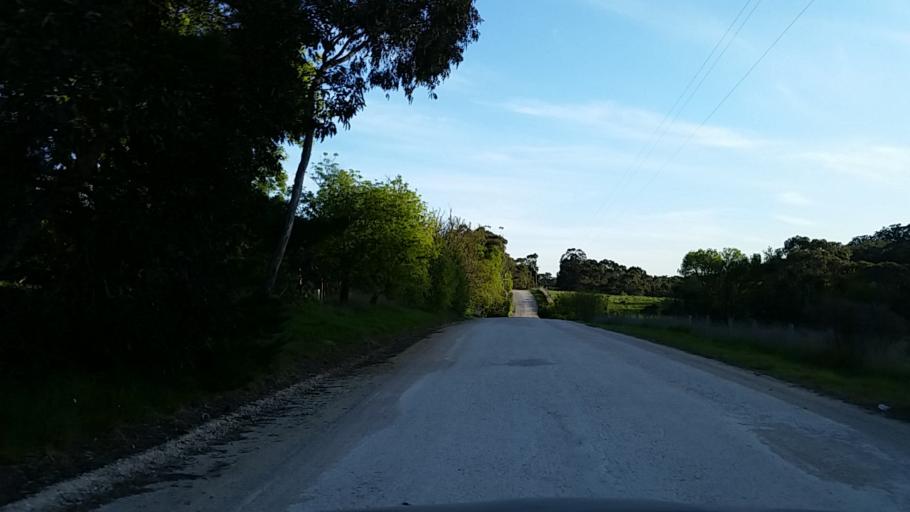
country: AU
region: South Australia
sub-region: Alexandrina
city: Mount Compass
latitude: -35.2899
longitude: 138.6897
